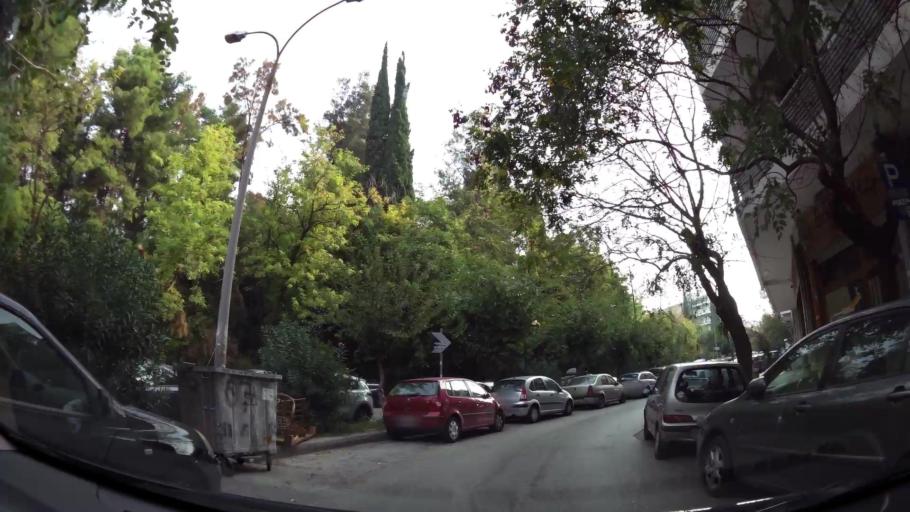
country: GR
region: Attica
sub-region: Nomarchia Athinas
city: Kipseli
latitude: 37.9933
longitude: 23.7429
